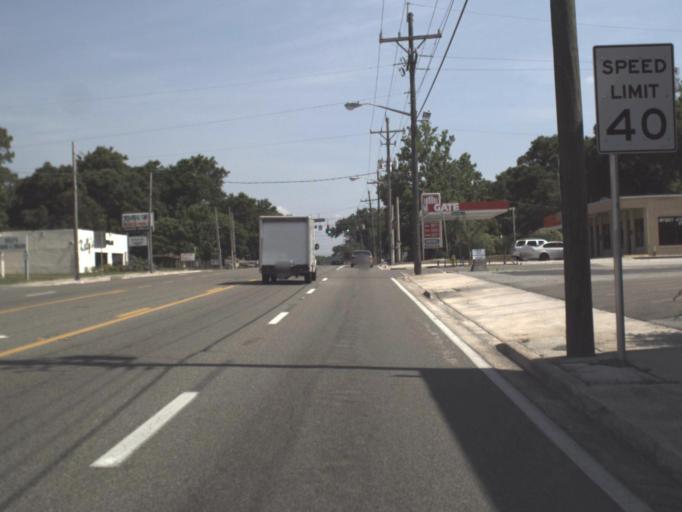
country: US
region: Florida
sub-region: Duval County
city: Jacksonville
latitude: 30.3373
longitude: -81.6025
